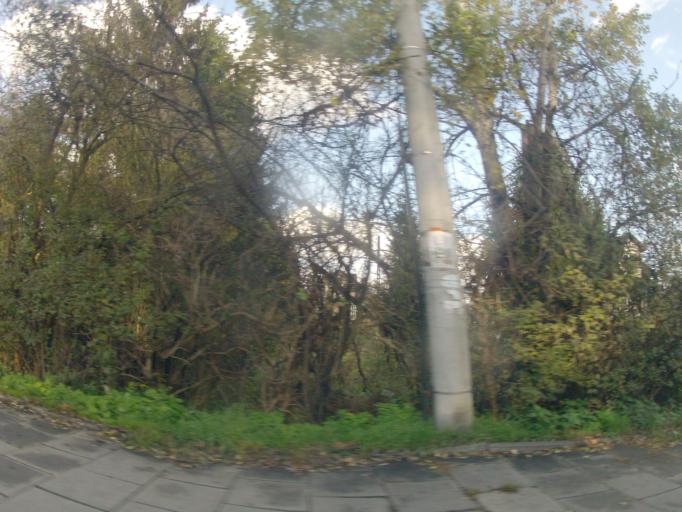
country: PL
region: Lesser Poland Voivodeship
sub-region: Powiat krakowski
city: Rzaska
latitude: 50.0695
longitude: 19.8598
